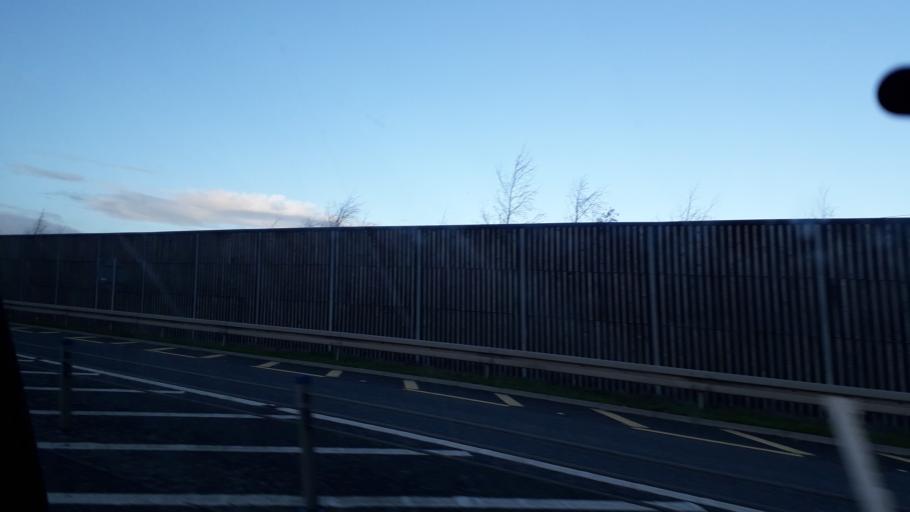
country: IE
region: Ulster
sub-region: County Monaghan
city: Castleblayney
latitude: 54.1133
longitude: -6.7547
